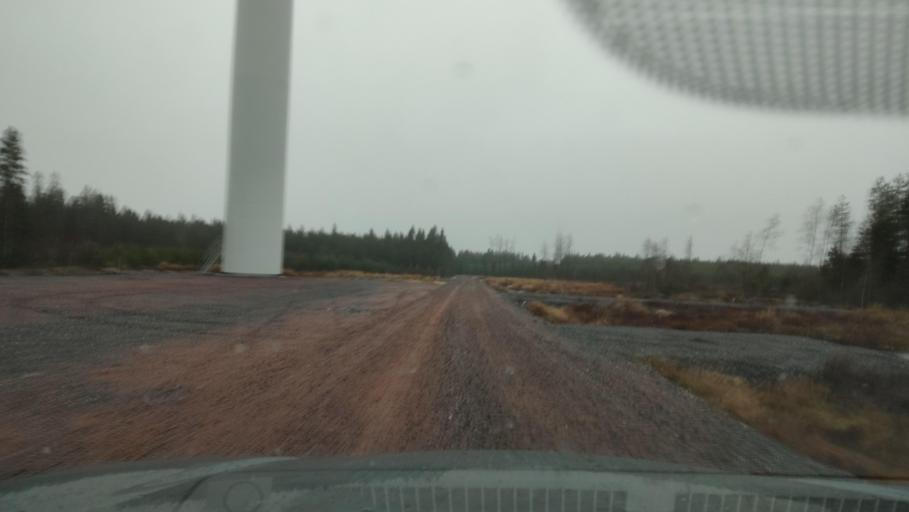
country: FI
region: Southern Ostrobothnia
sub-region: Suupohja
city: Karijoki
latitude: 62.1794
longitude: 21.7248
